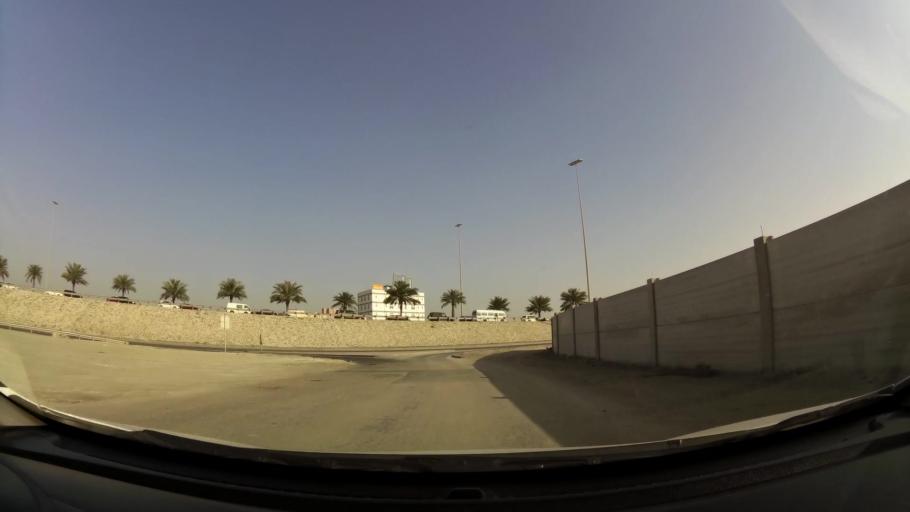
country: BH
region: Manama
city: Jidd Hafs
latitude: 26.2160
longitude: 50.5199
